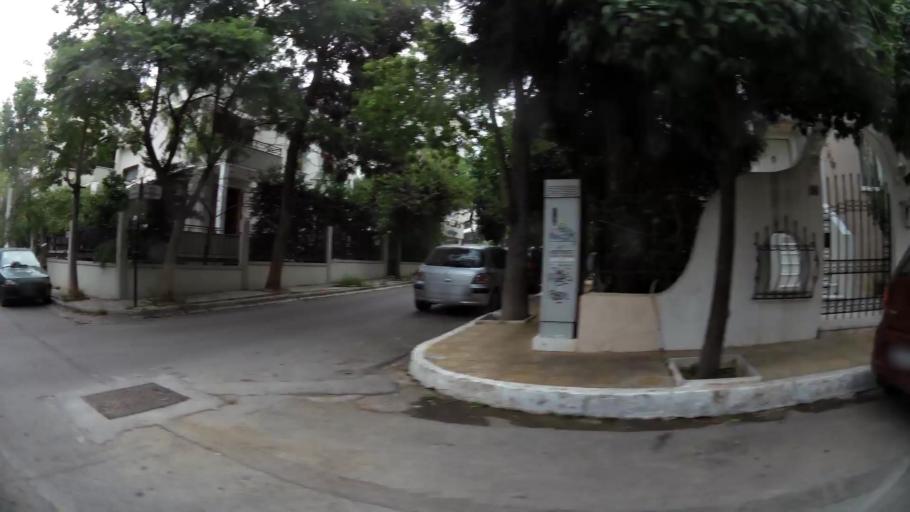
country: GR
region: Attica
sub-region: Nomarchia Athinas
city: Alimos
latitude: 37.9180
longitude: 23.7133
